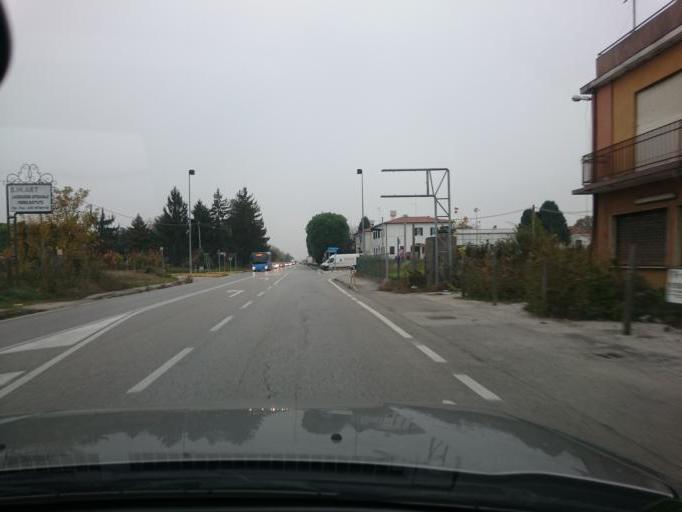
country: IT
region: Veneto
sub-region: Provincia di Padova
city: Sant'Angelo di Piove di Sacco
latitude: 45.3296
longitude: 11.9875
